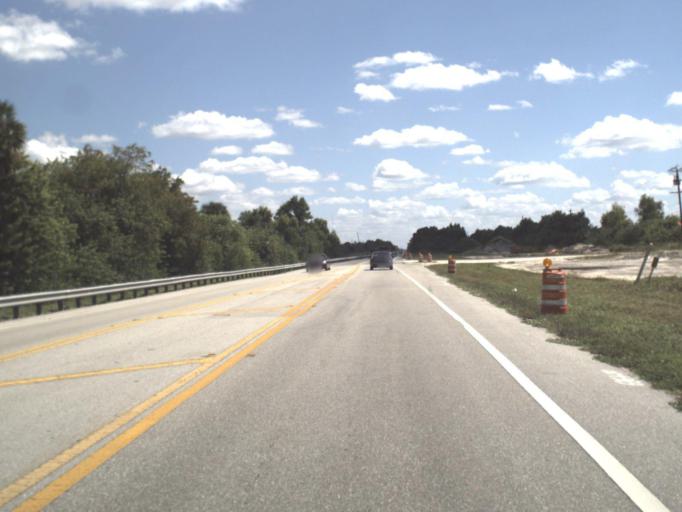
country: US
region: Florida
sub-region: Collier County
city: Lely Resort
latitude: 26.0337
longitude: -81.6529
